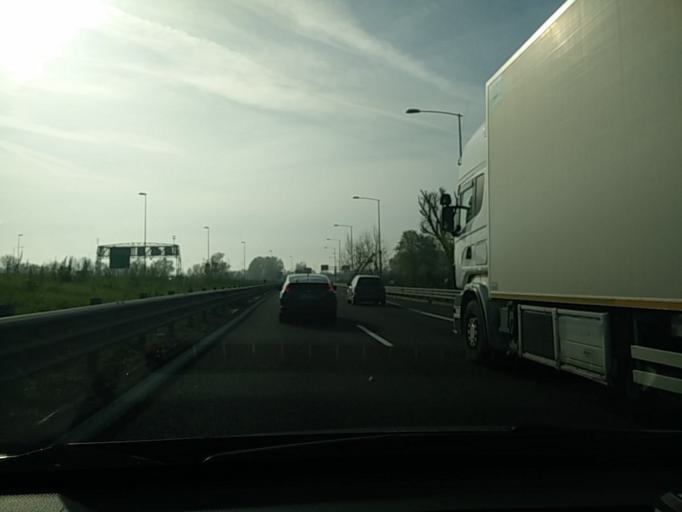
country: IT
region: Emilia-Romagna
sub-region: Provincia di Bologna
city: Bologna
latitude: 44.5180
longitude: 11.3729
